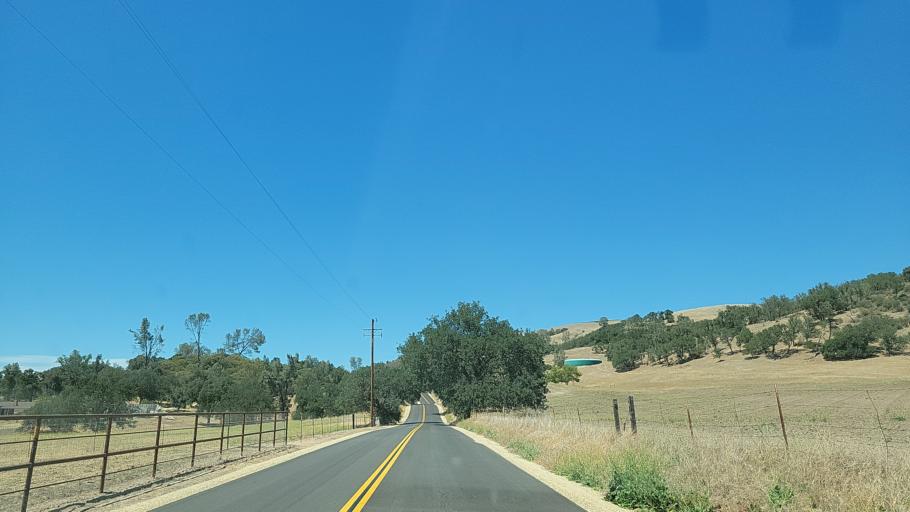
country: US
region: California
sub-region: San Luis Obispo County
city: Atascadero
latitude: 35.4721
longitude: -120.6235
